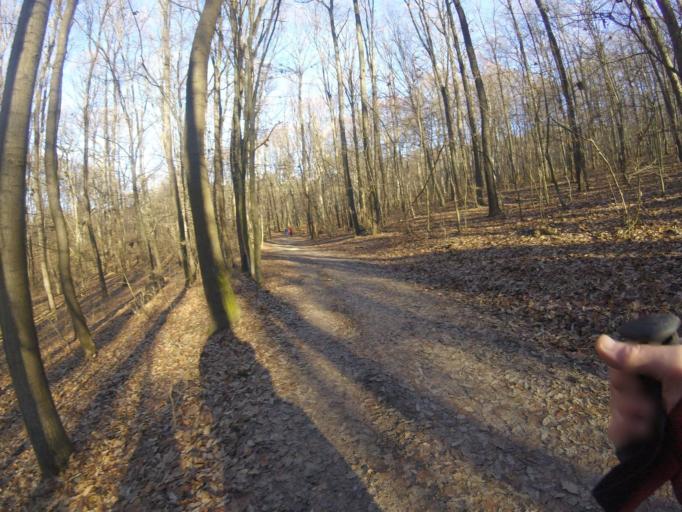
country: HU
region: Pest
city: Budakeszi
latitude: 47.5469
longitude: 18.9702
